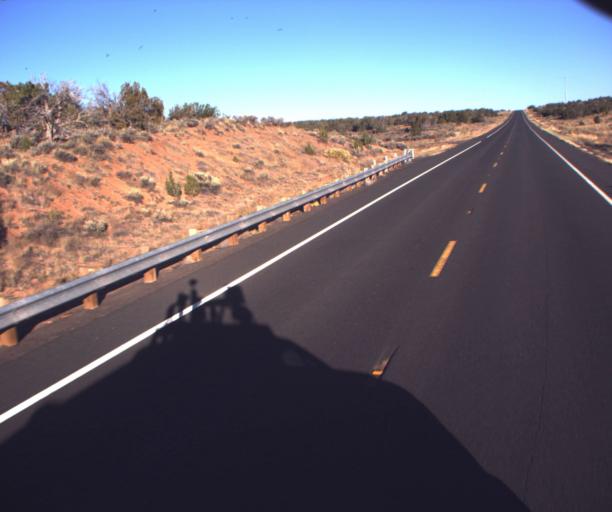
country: US
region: Arizona
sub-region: Apache County
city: Houck
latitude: 35.3386
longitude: -109.4461
